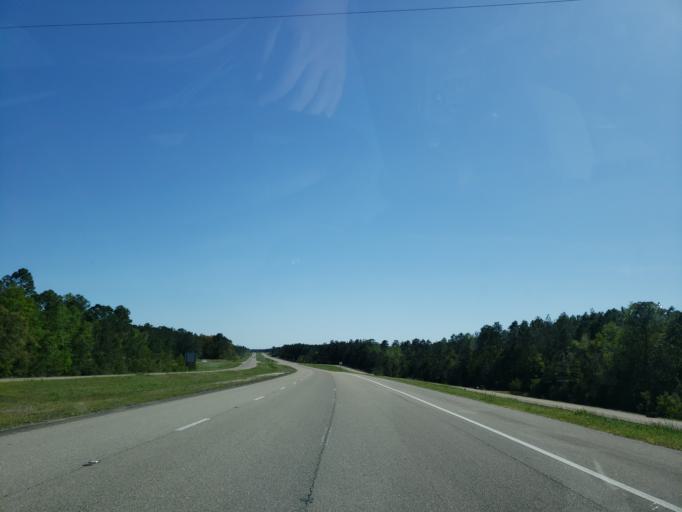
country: US
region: Mississippi
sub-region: Harrison County
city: Lyman
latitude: 30.5482
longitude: -89.0290
